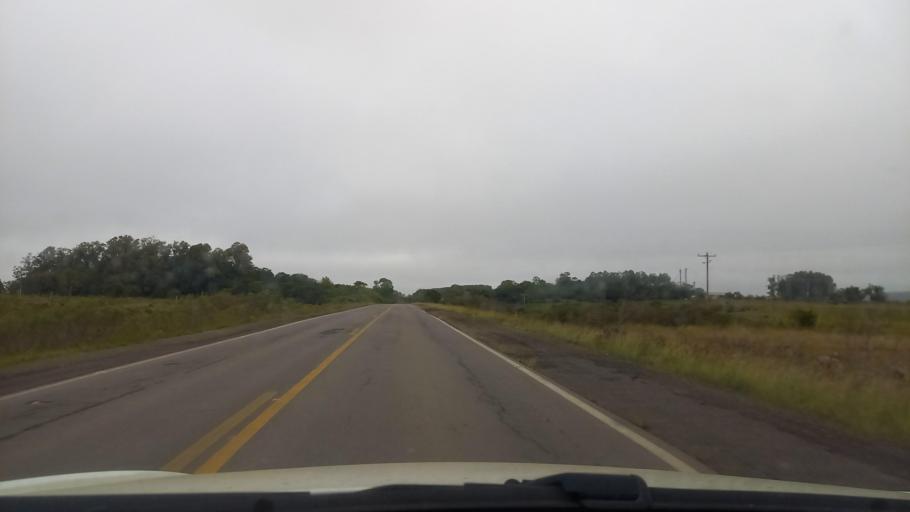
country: BR
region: Rio Grande do Sul
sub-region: Rosario Do Sul
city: Rosario do Sul
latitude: -30.1300
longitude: -54.6566
